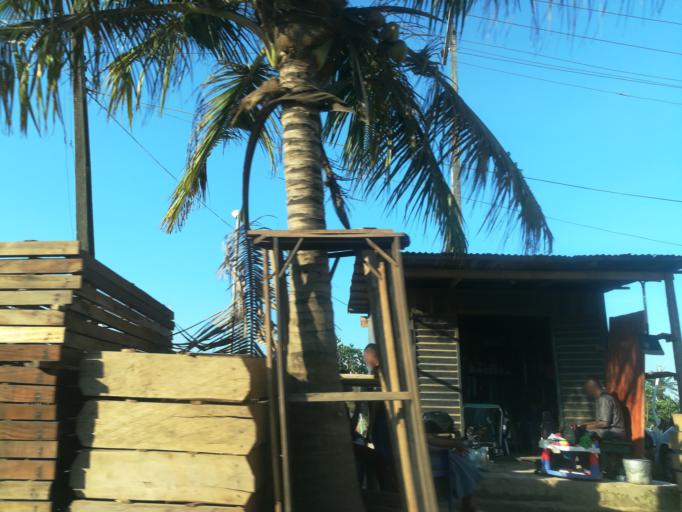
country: NG
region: Lagos
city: Ikorodu
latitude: 6.5857
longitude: 3.5232
